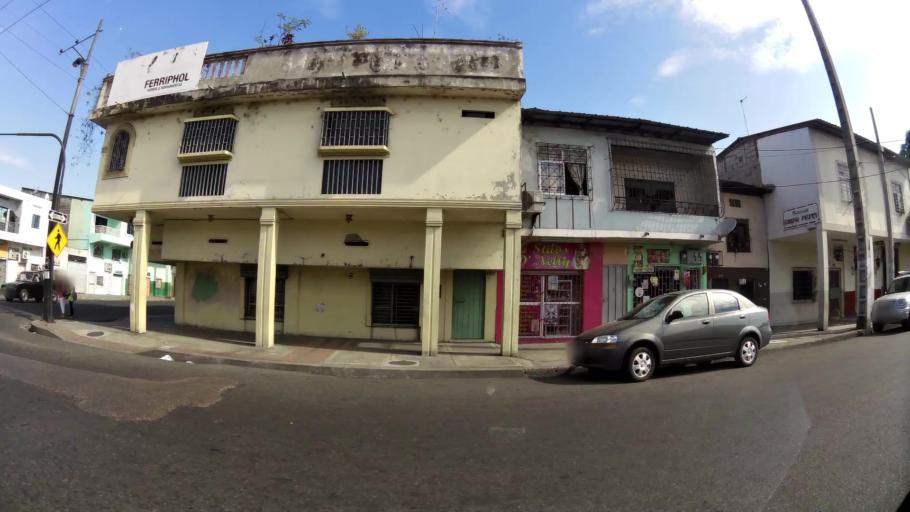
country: EC
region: Guayas
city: Guayaquil
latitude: -2.2155
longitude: -79.9061
